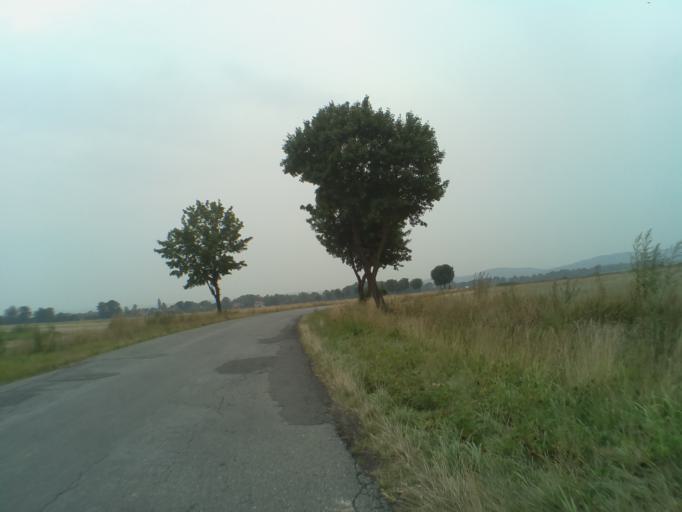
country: PL
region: Lower Silesian Voivodeship
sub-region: Powiat swidnicki
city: Swiebodzice
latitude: 50.9102
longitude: 16.3200
